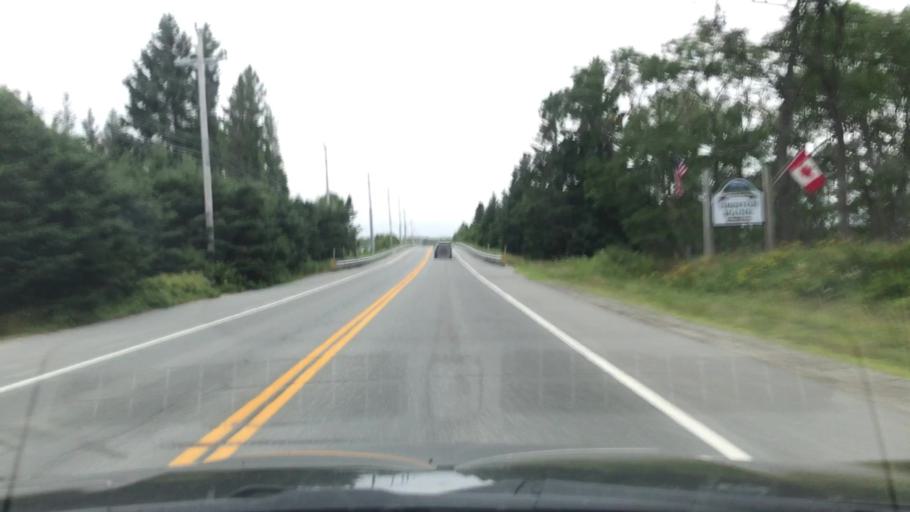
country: US
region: Maine
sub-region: Hancock County
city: Trenton
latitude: 44.4277
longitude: -68.3664
